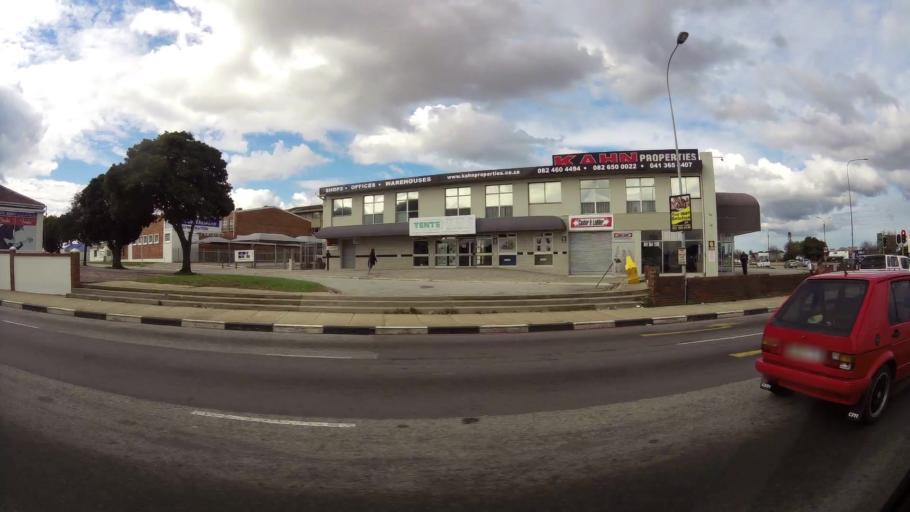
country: ZA
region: Eastern Cape
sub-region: Nelson Mandela Bay Metropolitan Municipality
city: Port Elizabeth
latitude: -33.9473
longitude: 25.5552
